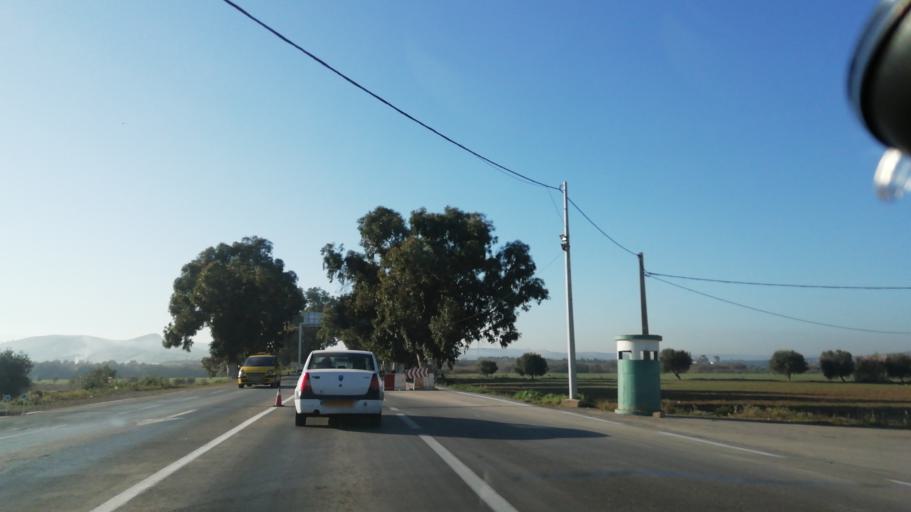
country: DZ
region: Tlemcen
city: Remchi
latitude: 35.0452
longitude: -1.5042
